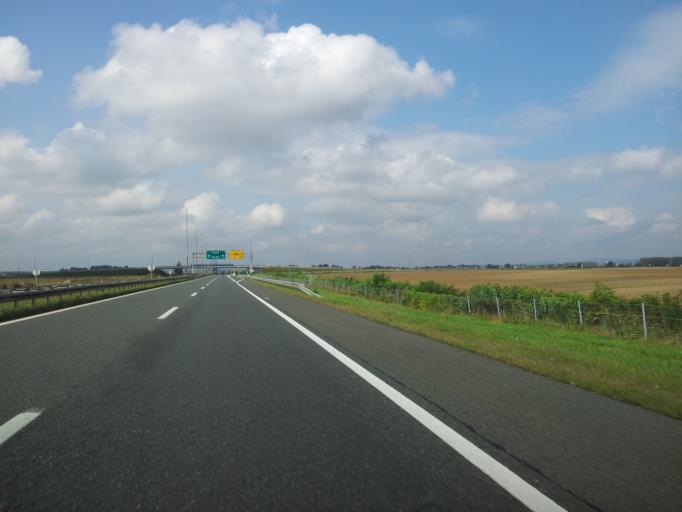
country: HR
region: Brodsko-Posavska
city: Ljupina
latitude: 45.2281
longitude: 17.4182
